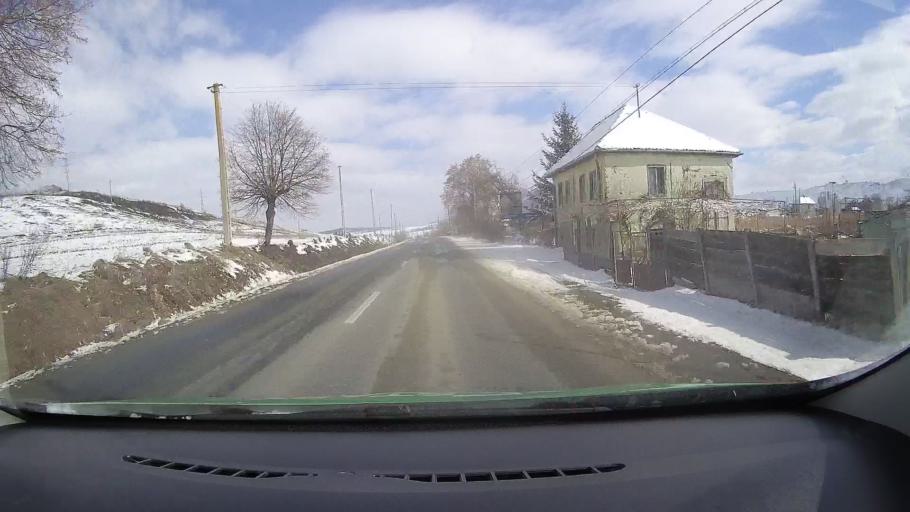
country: RO
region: Sibiu
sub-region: Oras Agnita
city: Agnita
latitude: 45.9645
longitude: 24.5893
